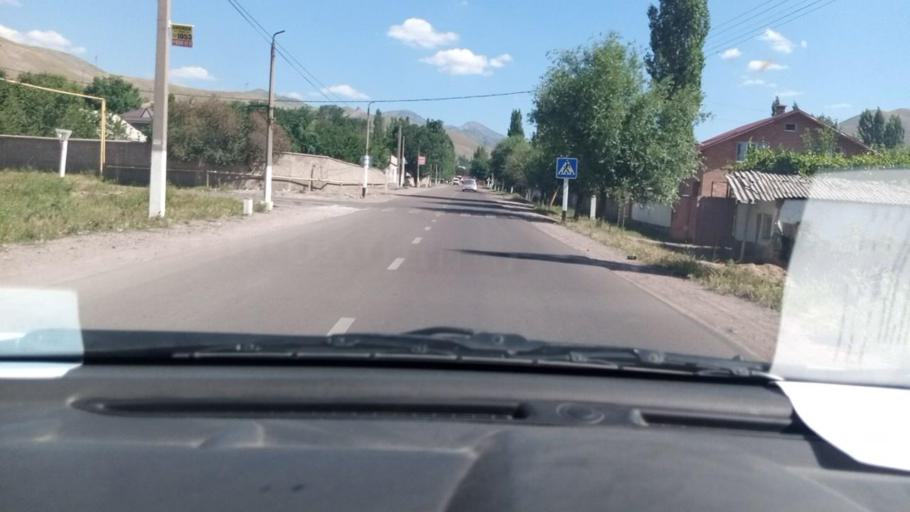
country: UZ
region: Toshkent
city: Angren
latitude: 41.0512
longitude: 70.0877
